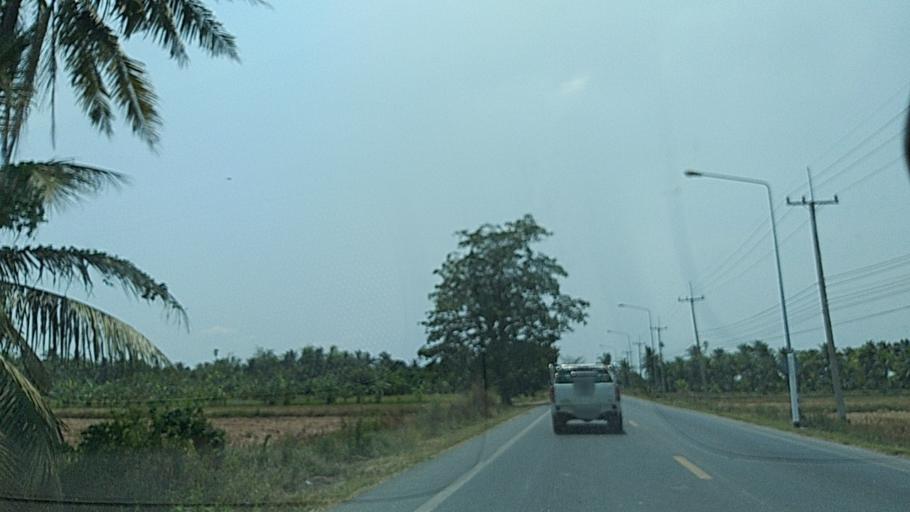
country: TH
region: Chachoengsao
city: Bang Nam Priao
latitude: 13.8755
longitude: 100.9677
